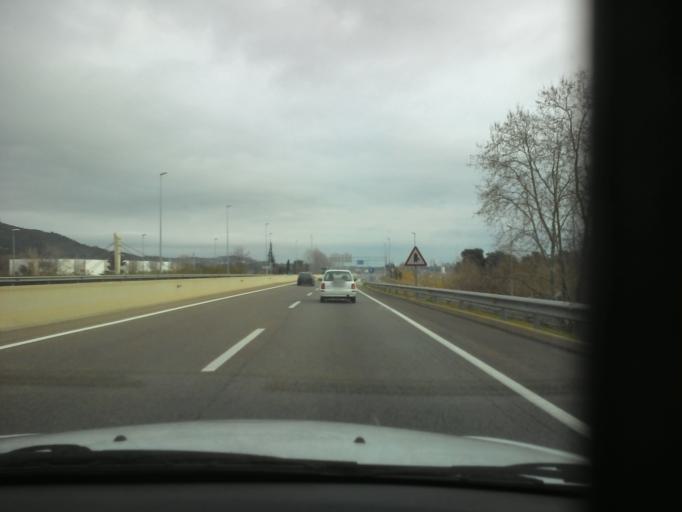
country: ES
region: Catalonia
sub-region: Provincia de Girona
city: Sant Feliu de Guixols
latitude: 41.8086
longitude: 3.0352
